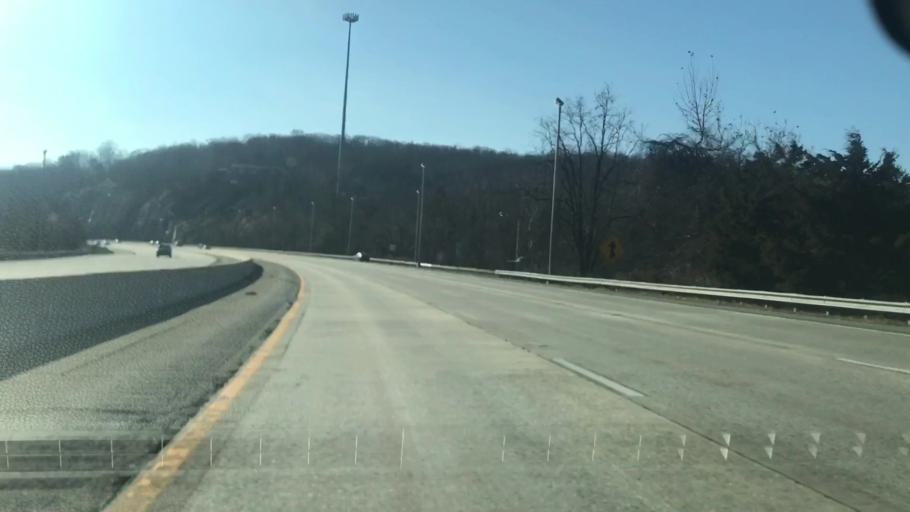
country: US
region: New Jersey
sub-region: Passaic County
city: Pompton Lakes
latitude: 41.0154
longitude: -74.2962
